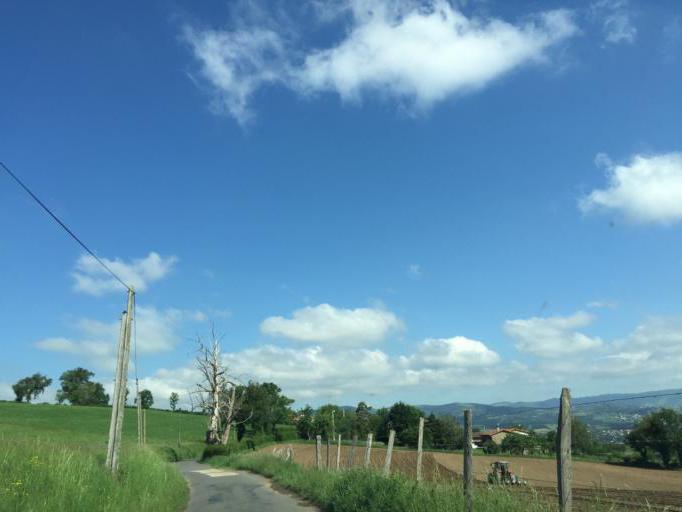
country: FR
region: Rhone-Alpes
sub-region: Departement de la Loire
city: Saint-Chamond
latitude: 45.4574
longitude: 4.5419
